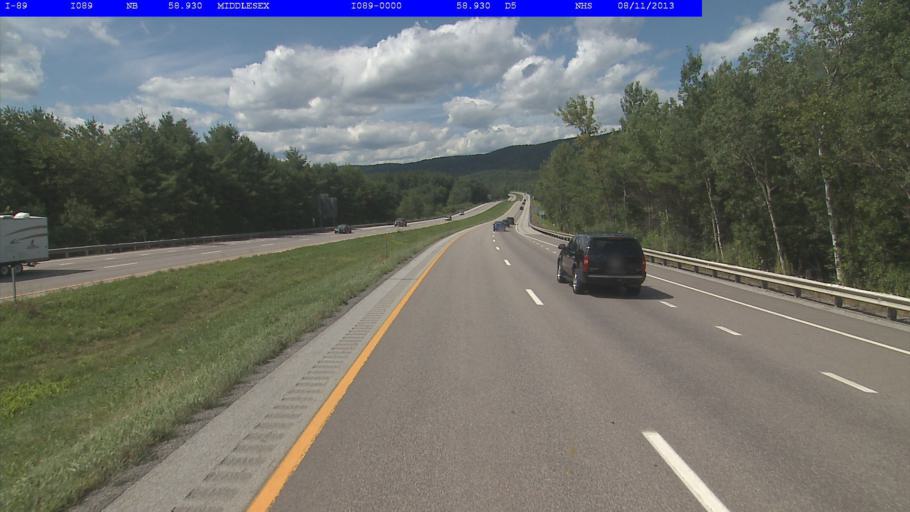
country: US
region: Vermont
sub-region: Washington County
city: Waterbury
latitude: 44.3007
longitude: -72.6879
